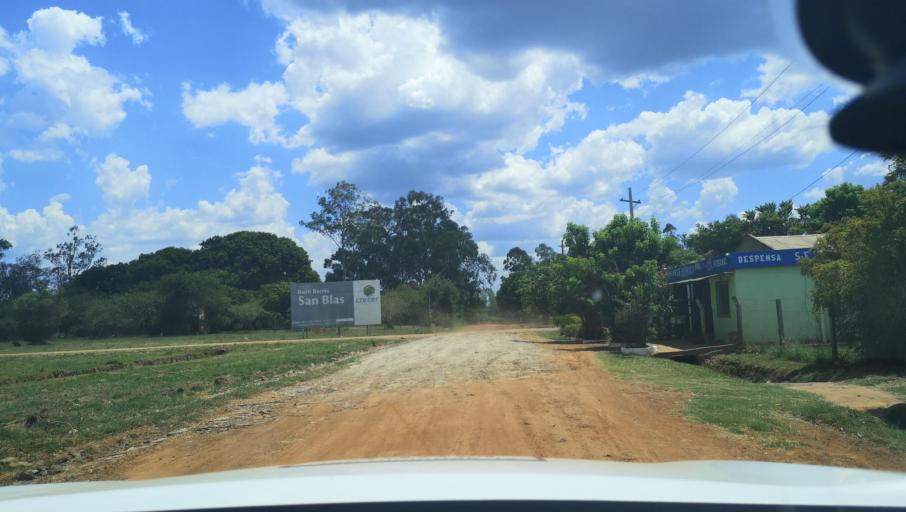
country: PY
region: Itapua
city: Carmen del Parana
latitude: -27.1718
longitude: -56.2374
